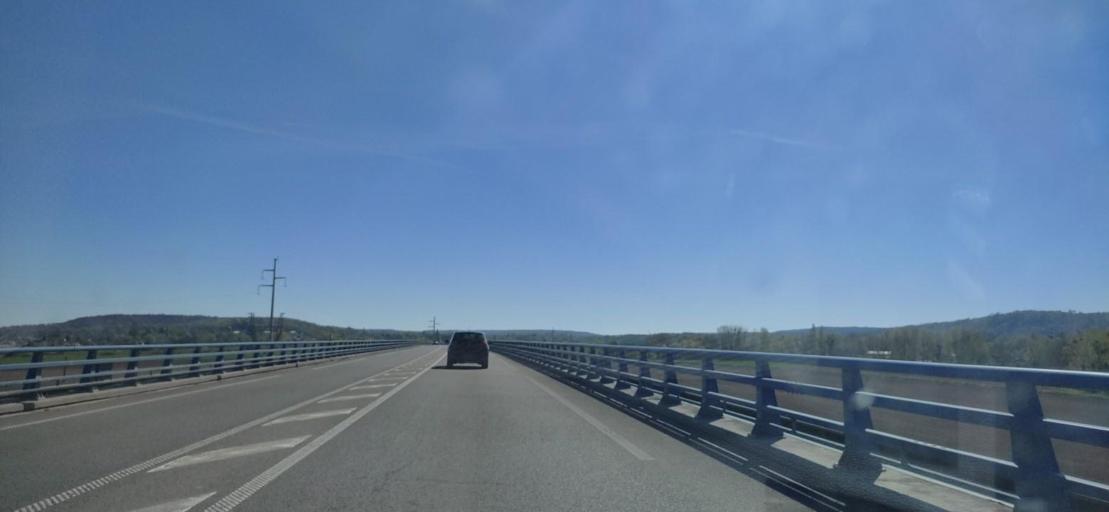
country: FR
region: Picardie
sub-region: Departement de l'Oise
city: Clairoix
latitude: 49.4356
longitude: 2.8548
